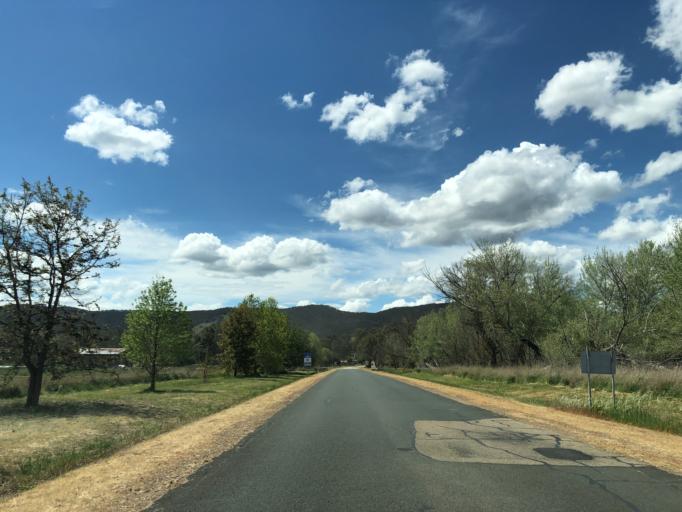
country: AU
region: Victoria
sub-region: Benalla
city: Benalla
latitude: -36.7335
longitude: 146.1037
